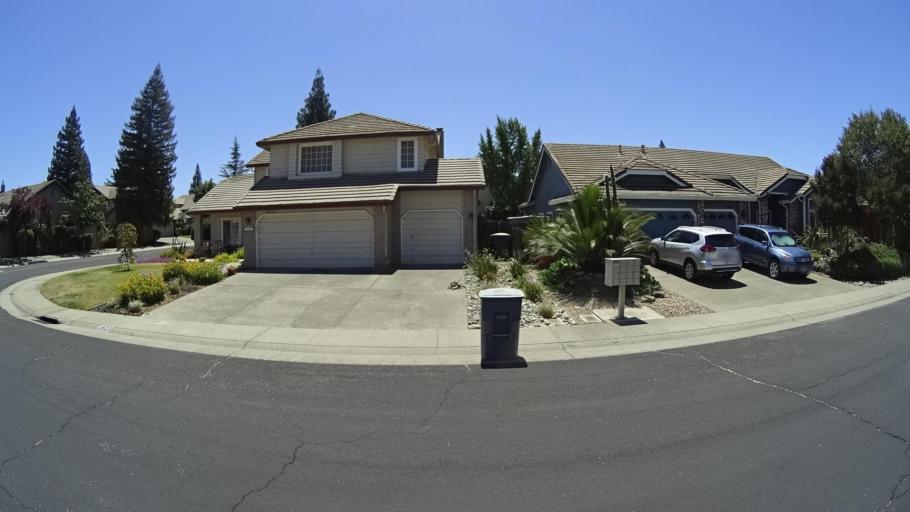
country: US
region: California
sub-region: Placer County
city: Rocklin
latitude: 38.8091
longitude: -121.2708
